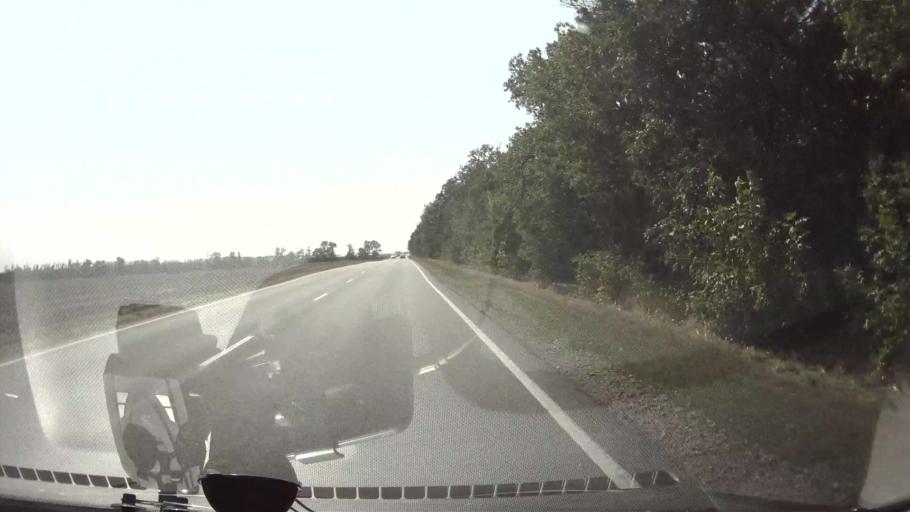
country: RU
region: Krasnodarskiy
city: Kavkazskaya
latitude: 45.5029
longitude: 40.6804
